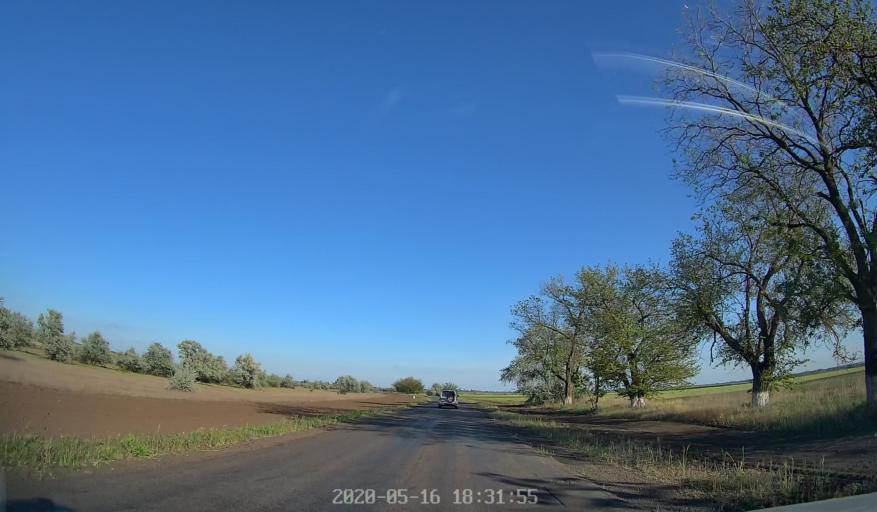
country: UA
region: Odessa
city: Lymanske
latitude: 46.5409
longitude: 30.0474
